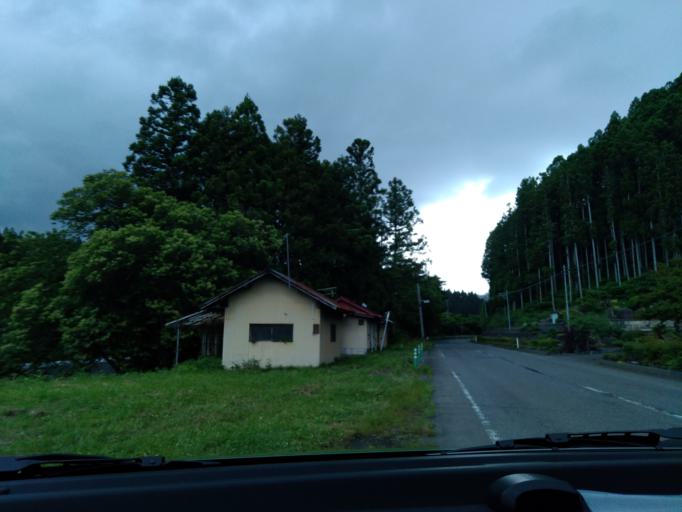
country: JP
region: Iwate
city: Ichinoseki
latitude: 38.8251
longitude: 140.9109
